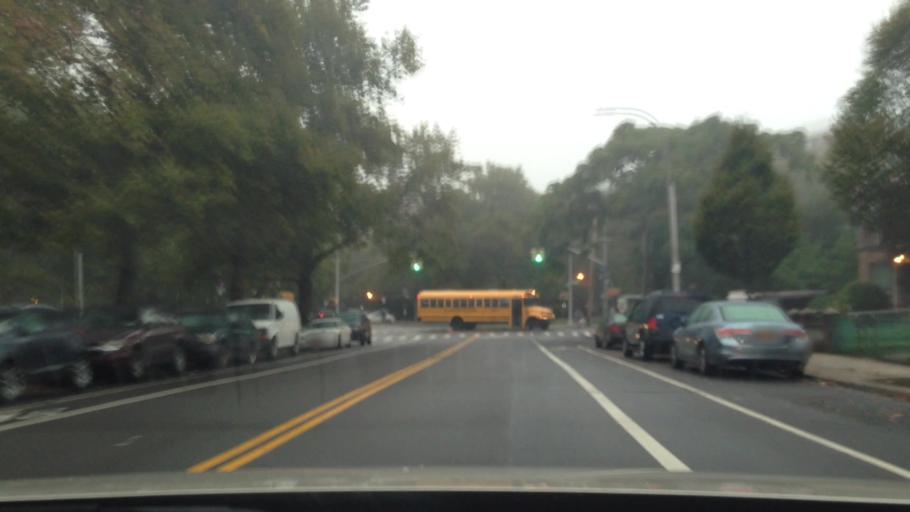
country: US
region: New York
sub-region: Kings County
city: East New York
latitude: 40.6555
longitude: -73.8824
